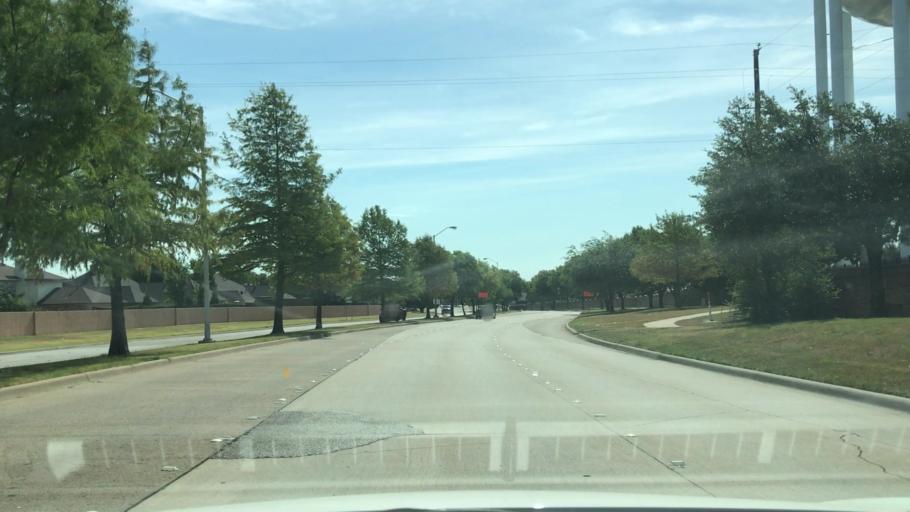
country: US
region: Texas
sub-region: Collin County
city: Plano
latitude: 33.0564
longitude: -96.7648
